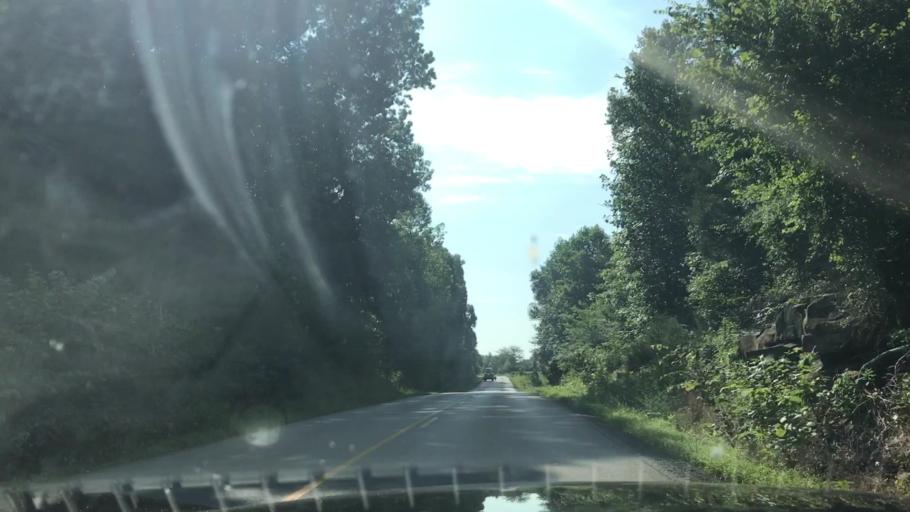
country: US
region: Kentucky
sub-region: Green County
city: Greensburg
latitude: 37.2258
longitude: -85.6679
